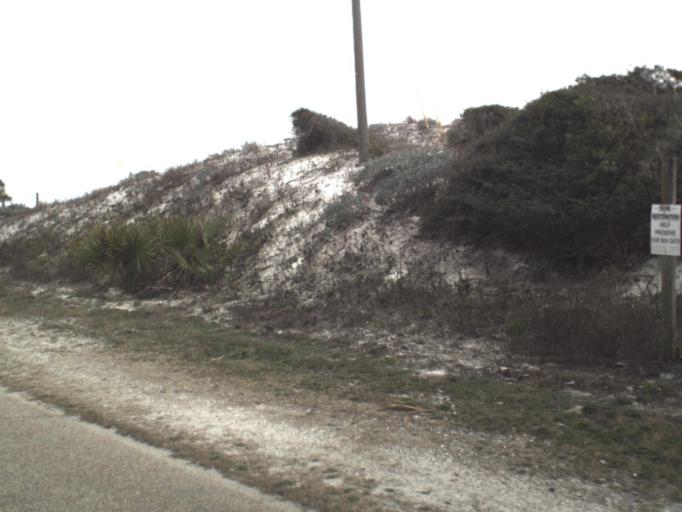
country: US
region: Florida
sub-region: Bay County
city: Laguna Beach
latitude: 30.2480
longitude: -85.9432
